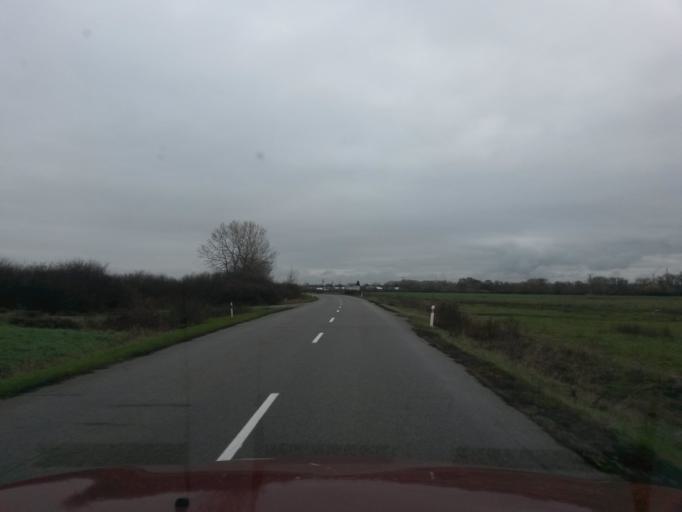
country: SK
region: Kosicky
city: Trebisov
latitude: 48.5495
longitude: 21.8990
